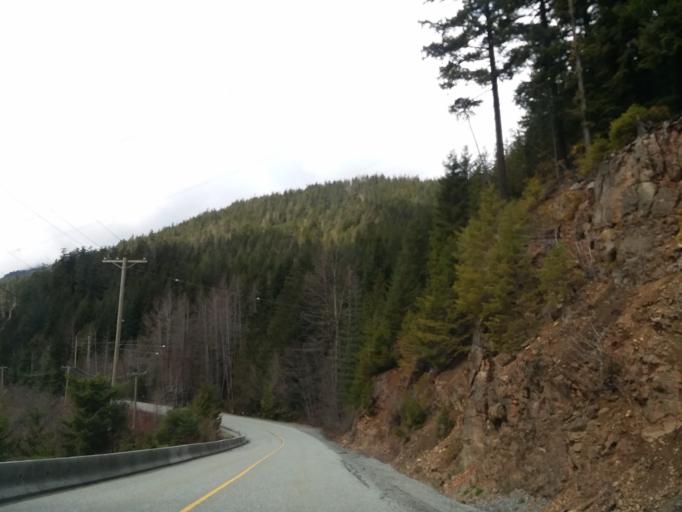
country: CA
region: British Columbia
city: Whistler
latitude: 50.0946
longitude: -123.0081
